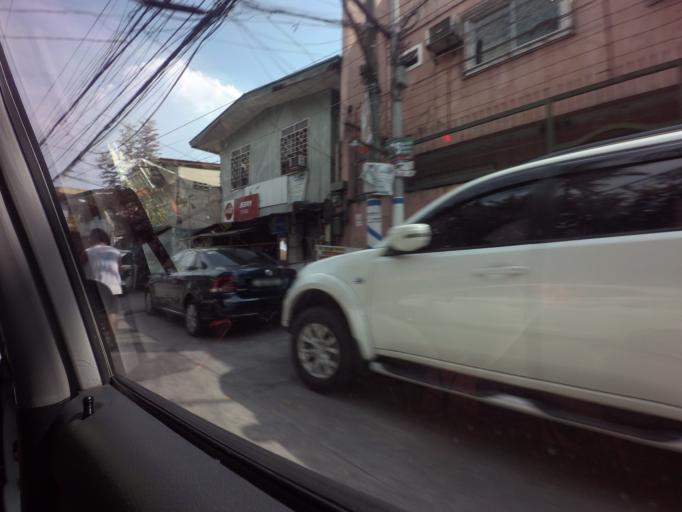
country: PH
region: Metro Manila
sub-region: San Juan
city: San Juan
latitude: 14.6011
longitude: 121.0151
